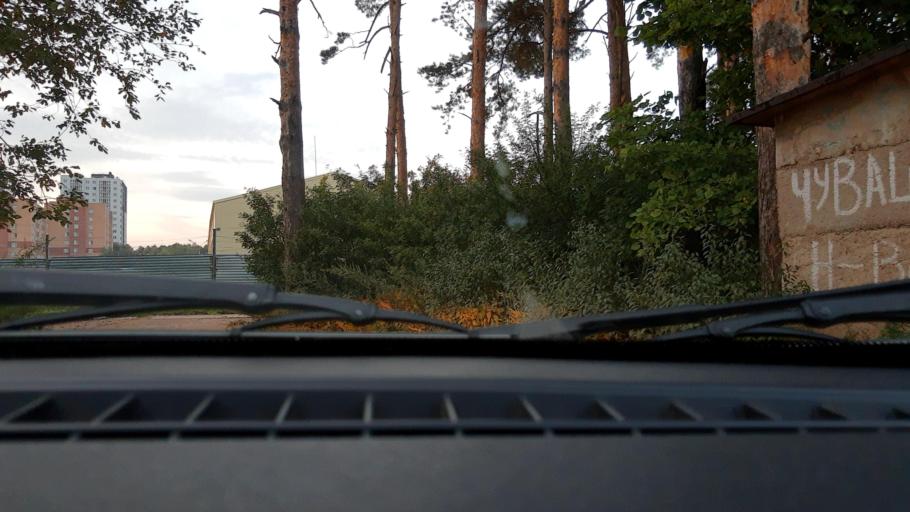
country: RU
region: Bashkortostan
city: Mikhaylovka
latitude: 54.7889
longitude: 55.8555
